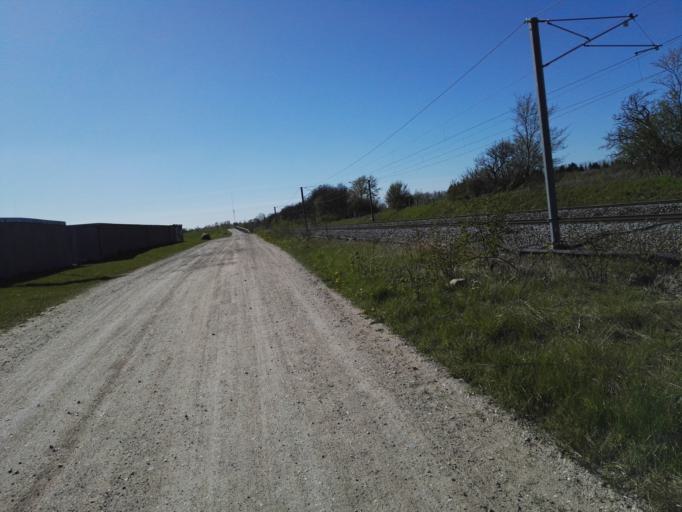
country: DK
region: Capital Region
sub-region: Egedal Kommune
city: Smorumnedre
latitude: 55.7523
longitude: 12.2800
